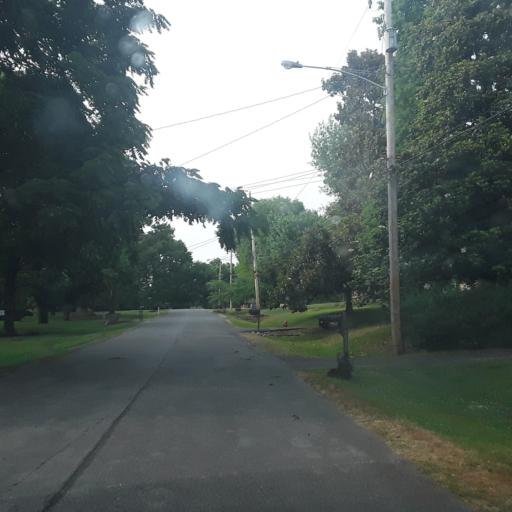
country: US
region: Tennessee
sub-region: Davidson County
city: Oak Hill
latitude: 36.0689
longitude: -86.7522
